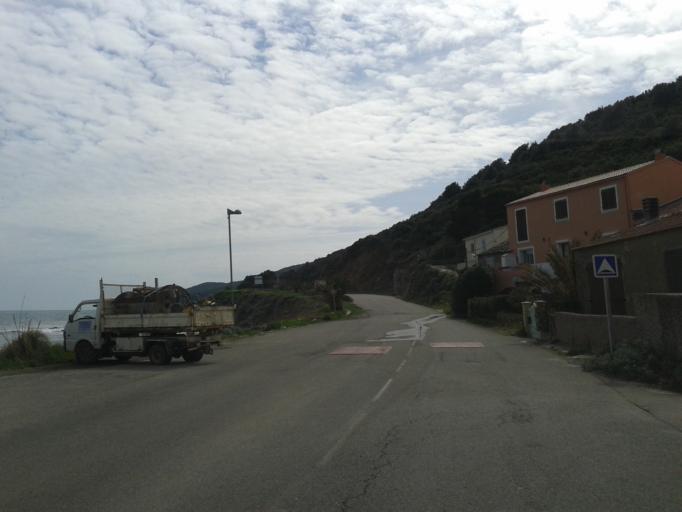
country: FR
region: Corsica
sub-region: Departement de la Haute-Corse
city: Brando
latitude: 42.9569
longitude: 9.4550
